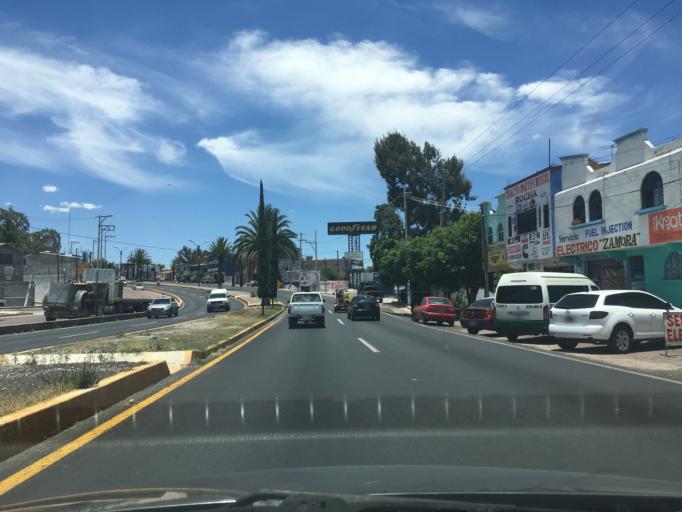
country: MX
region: Hidalgo
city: Actopan
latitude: 20.2640
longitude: -98.9467
